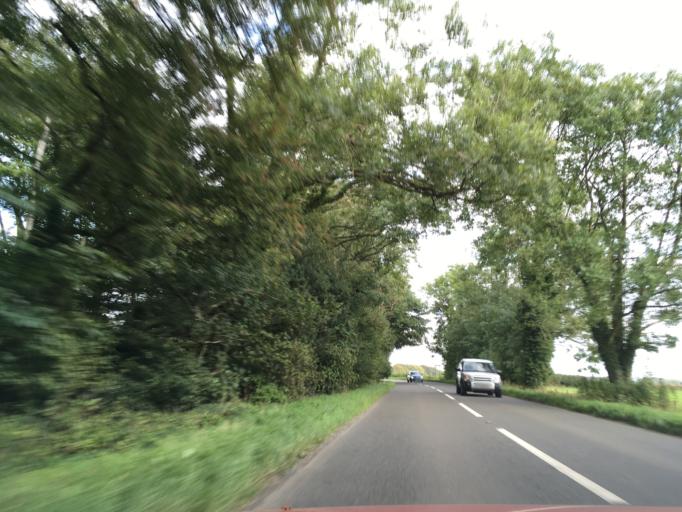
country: GB
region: England
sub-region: Gloucestershire
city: Dursley
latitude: 51.6672
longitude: -2.2922
